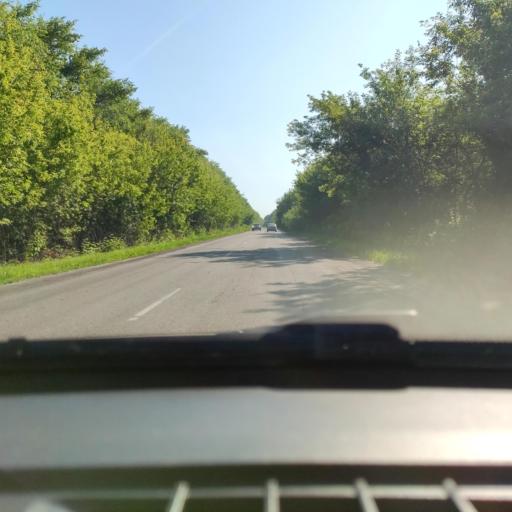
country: RU
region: Voronezj
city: Panino
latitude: 51.6222
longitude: 40.0288
